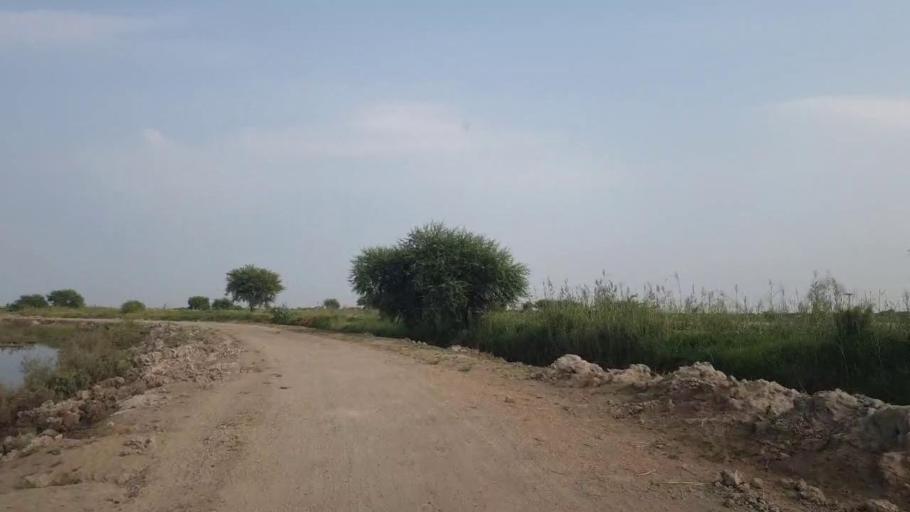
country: PK
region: Sindh
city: Kadhan
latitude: 24.4586
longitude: 68.8077
